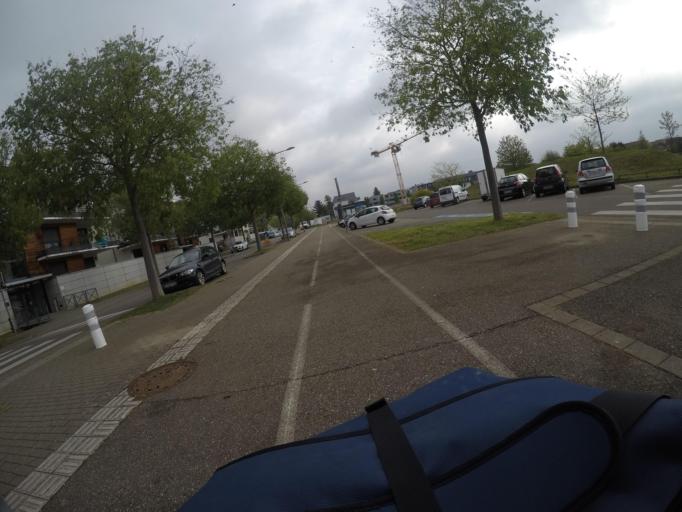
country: FR
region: Alsace
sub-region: Departement du Bas-Rhin
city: Oberhausbergen
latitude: 48.6080
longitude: 7.6864
